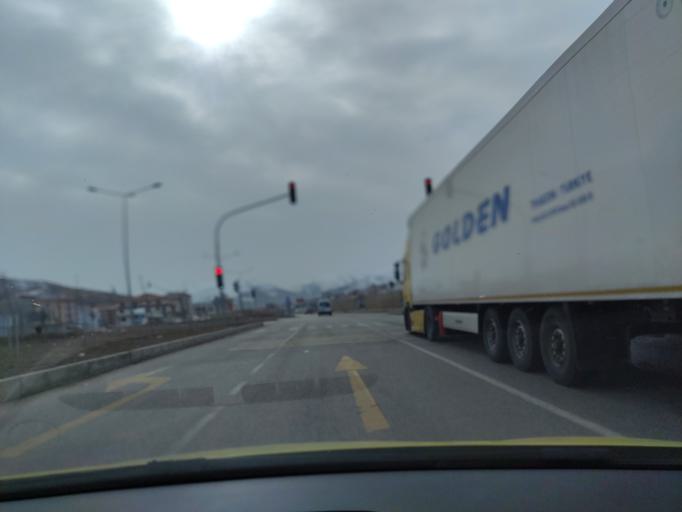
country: TR
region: Bayburt
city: Bayburt
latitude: 40.2656
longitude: 40.2036
